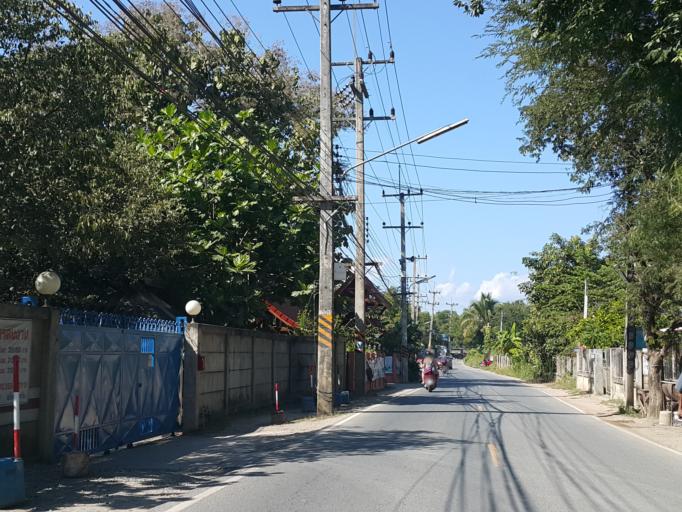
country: TH
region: Chiang Mai
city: San Sai
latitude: 18.9396
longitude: 98.9310
